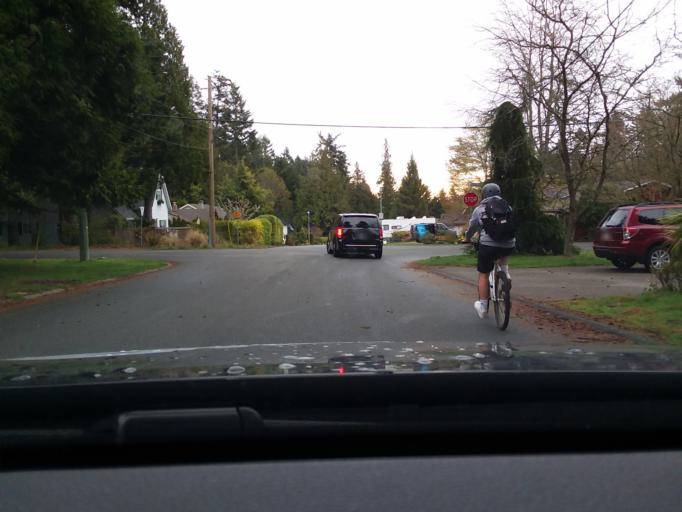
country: CA
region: British Columbia
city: Victoria
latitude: 48.5231
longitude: -123.3798
